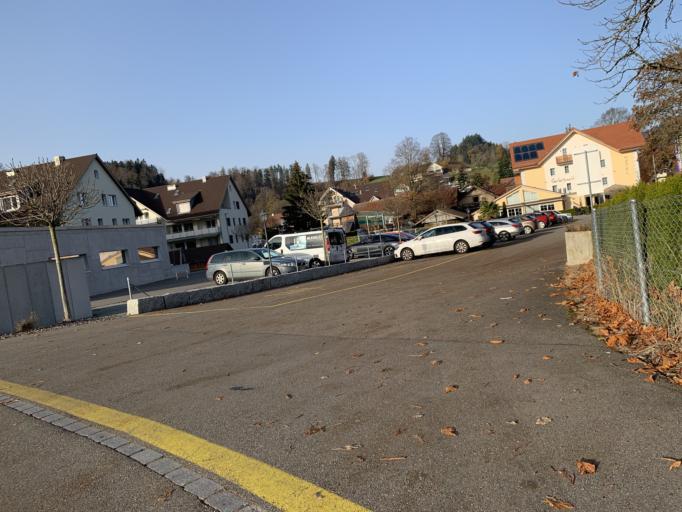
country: CH
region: Zurich
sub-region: Bezirk Hinwil
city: Wald
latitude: 47.3128
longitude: 8.9136
